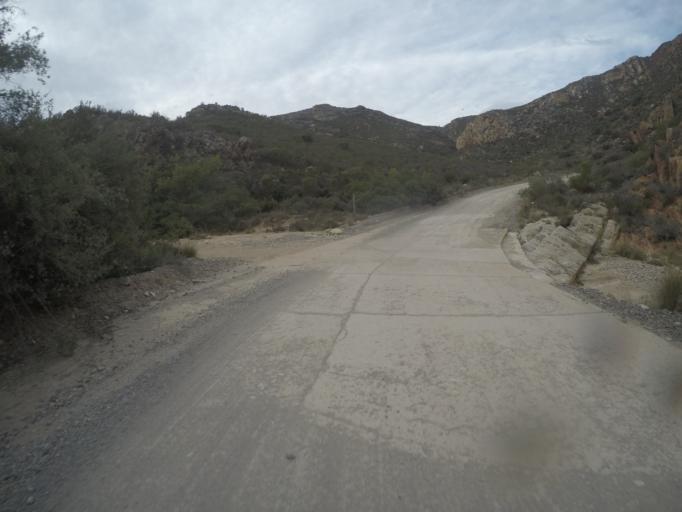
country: ZA
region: Eastern Cape
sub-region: Cacadu District Municipality
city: Willowmore
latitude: -33.5081
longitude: 23.6371
